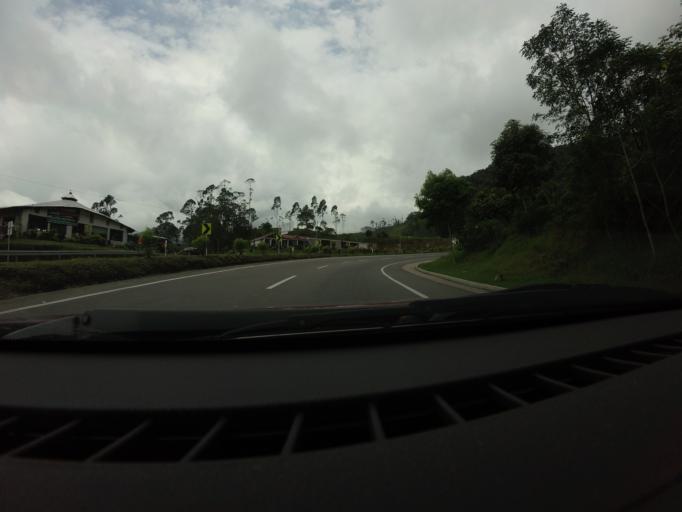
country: CO
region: Cundinamarca
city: San Francisco
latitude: 4.9455
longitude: -74.2920
